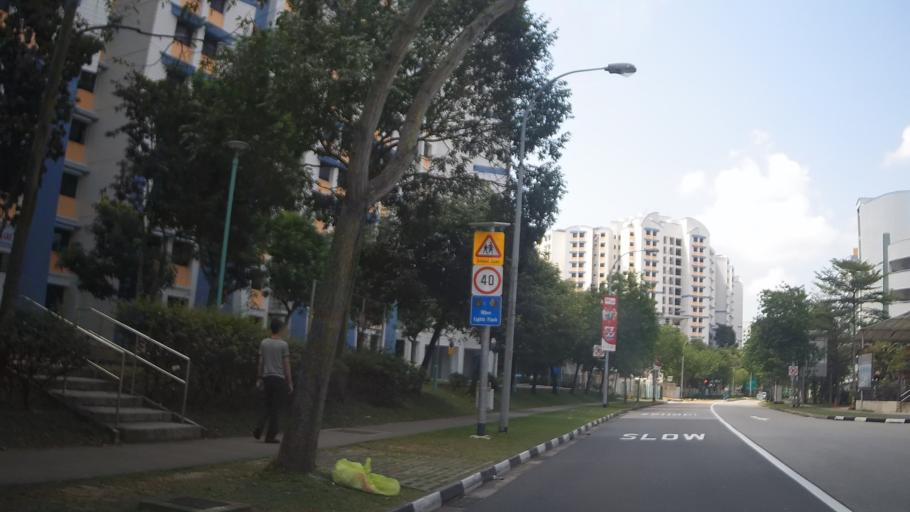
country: MY
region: Johor
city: Kampung Pasir Gudang Baru
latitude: 1.3938
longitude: 103.8906
